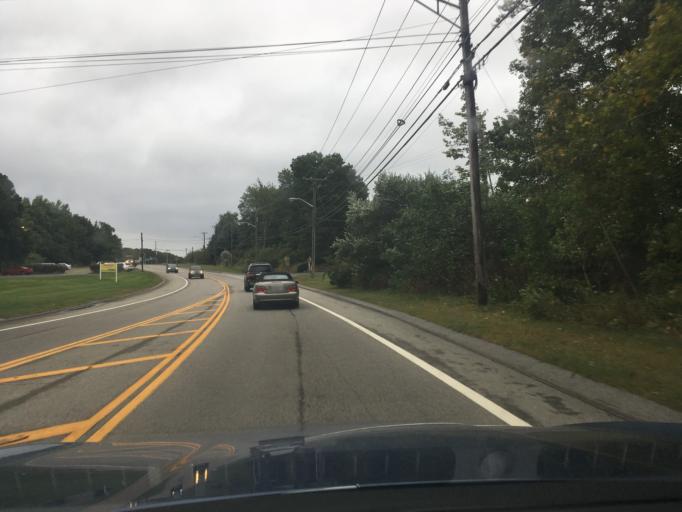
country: US
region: Rhode Island
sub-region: Washington County
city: Exeter
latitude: 41.5862
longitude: -71.5021
